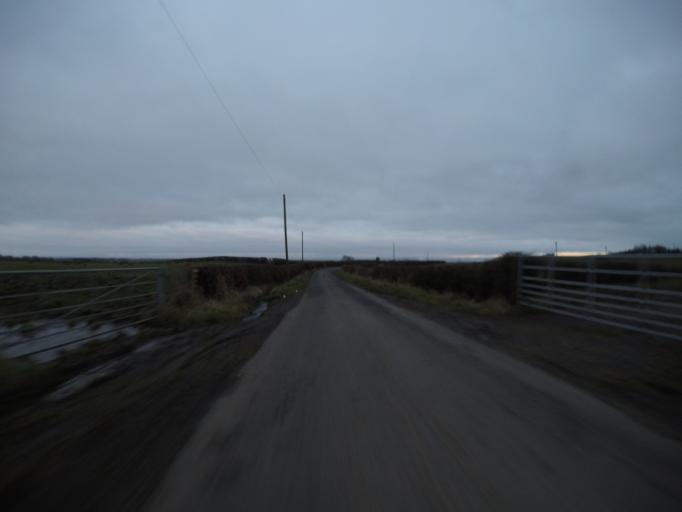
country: GB
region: Scotland
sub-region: North Ayrshire
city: Dalry
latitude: 55.6835
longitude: -4.7293
